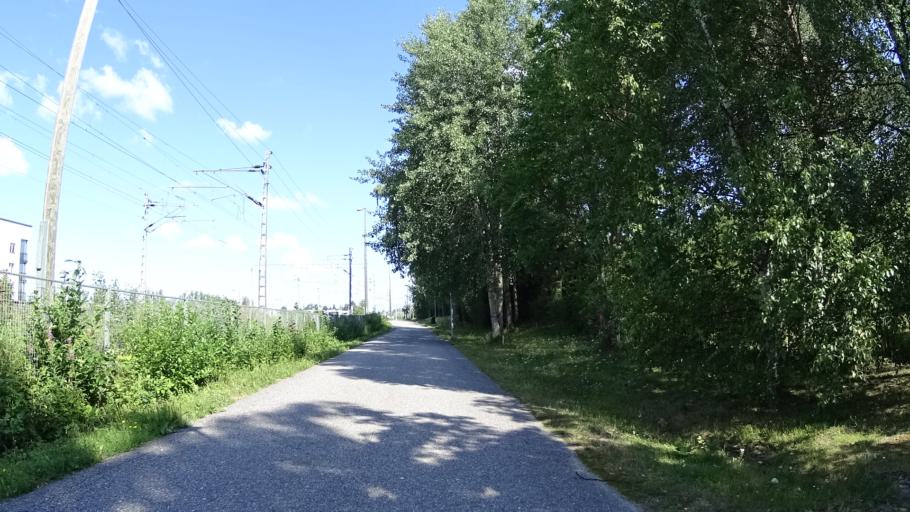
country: FI
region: Uusimaa
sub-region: Helsinki
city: Jaervenpaeae
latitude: 60.4617
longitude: 25.1005
